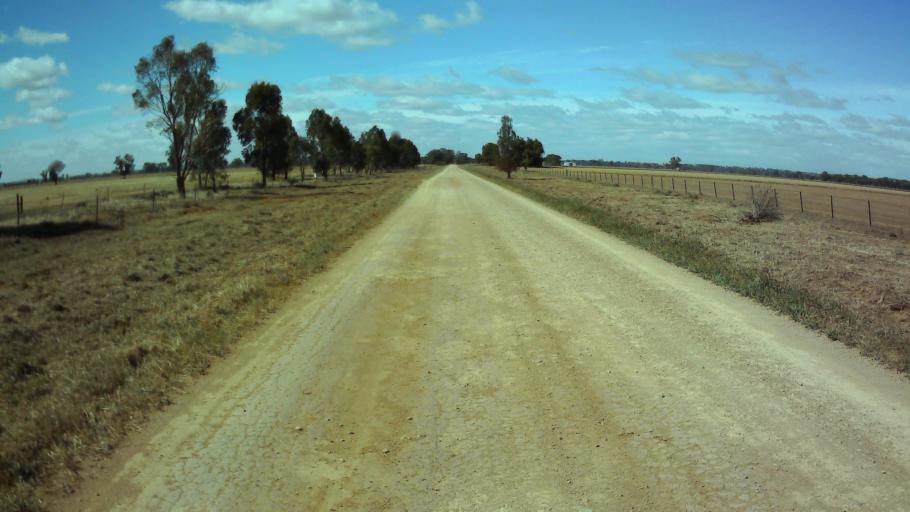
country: AU
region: New South Wales
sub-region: Weddin
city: Grenfell
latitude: -34.0185
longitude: 148.3195
